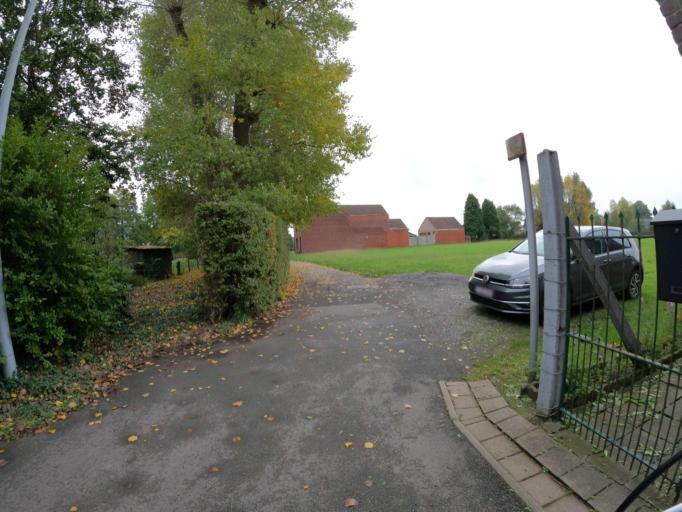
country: BE
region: Flanders
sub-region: Provincie West-Vlaanderen
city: Tielt
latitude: 50.9972
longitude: 3.3415
